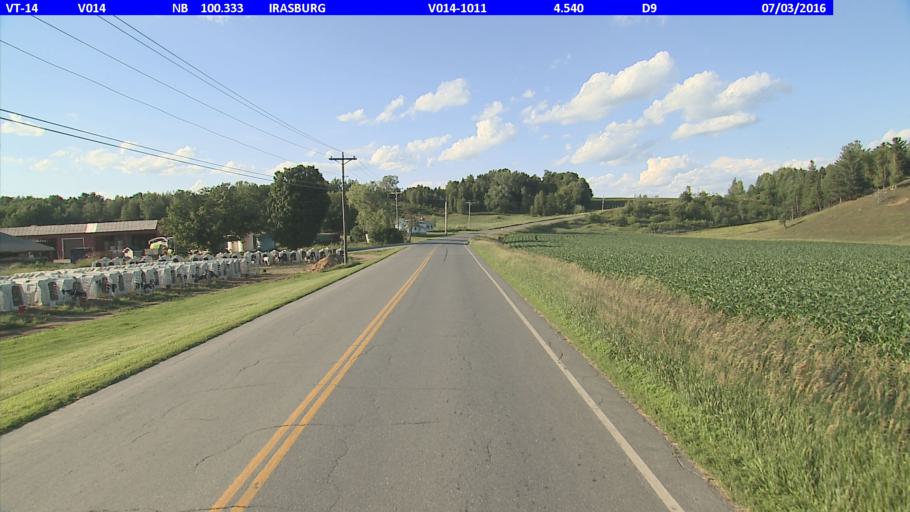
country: US
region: Vermont
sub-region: Orleans County
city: Newport
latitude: 44.8253
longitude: -72.2946
